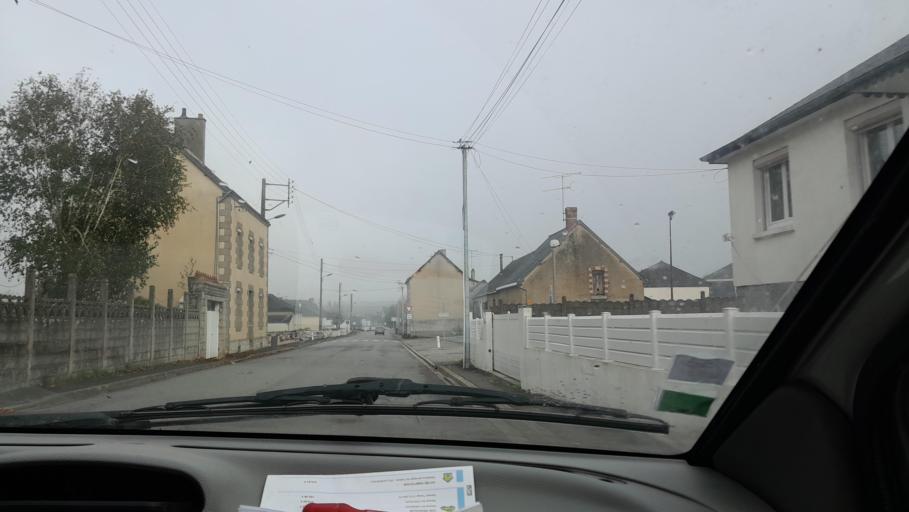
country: FR
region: Pays de la Loire
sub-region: Departement de la Mayenne
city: Saint-Pierre-la-Cour
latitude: 48.1111
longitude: -1.0246
